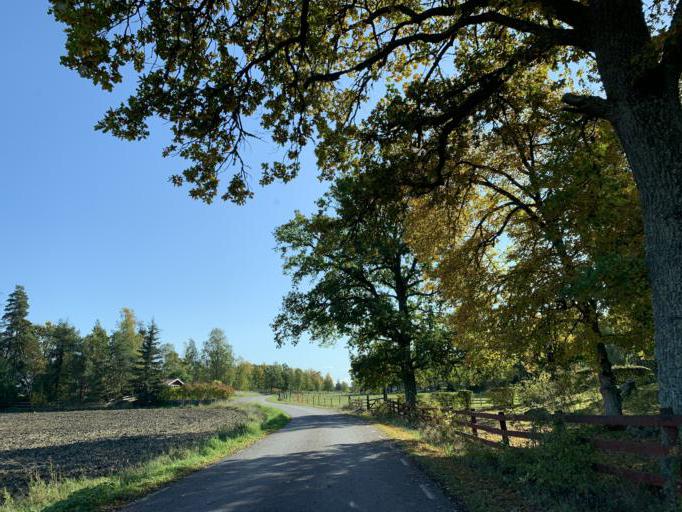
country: SE
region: Soedermanland
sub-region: Eskilstuna Kommun
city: Kvicksund
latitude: 59.5200
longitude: 16.3339
